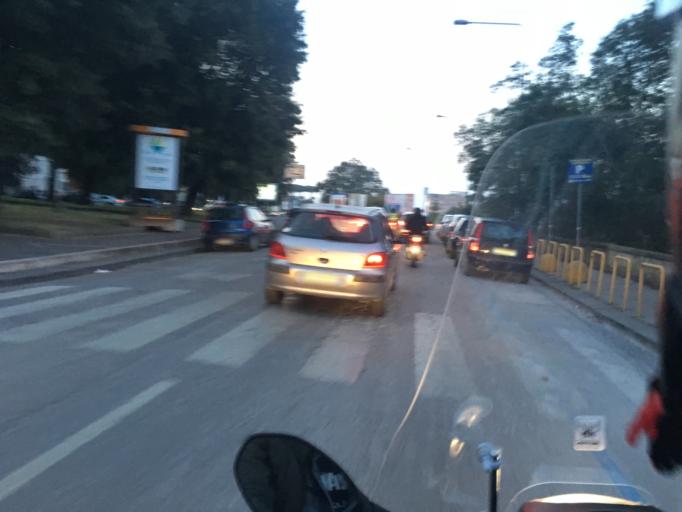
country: IT
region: Campania
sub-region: Provincia di Napoli
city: Napoli
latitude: 40.8650
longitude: 14.2272
